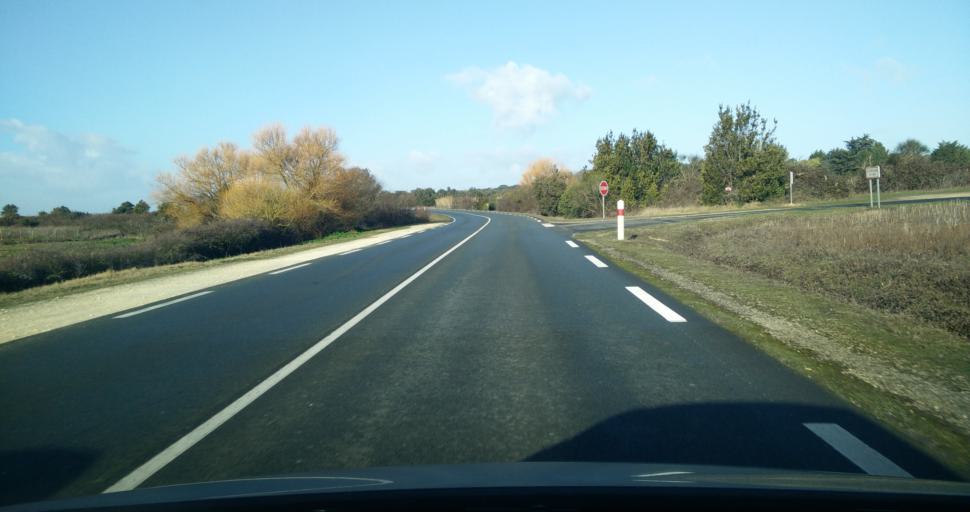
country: FR
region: Poitou-Charentes
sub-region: Departement de la Charente-Maritime
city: Rivedoux-Plage
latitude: 46.1518
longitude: -1.2786
